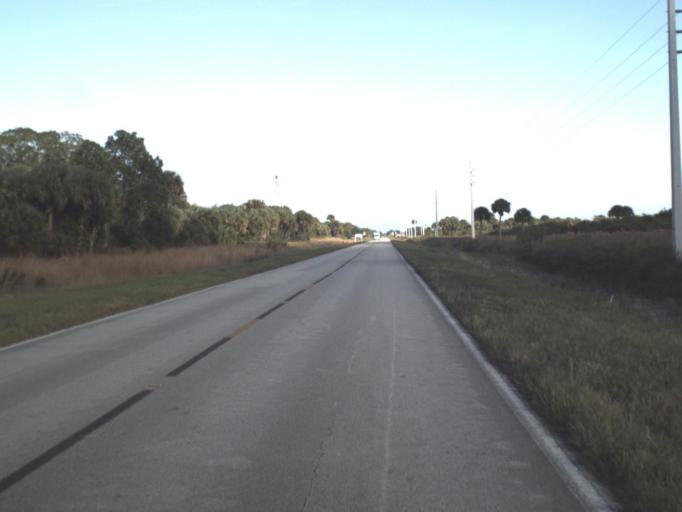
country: US
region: Florida
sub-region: Brevard County
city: Titusville
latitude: 28.6436
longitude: -80.7067
